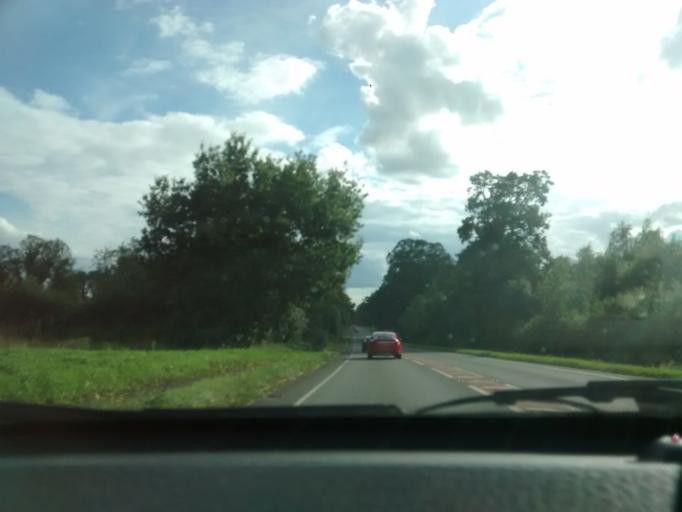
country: GB
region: England
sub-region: Norfolk
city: Downham Market
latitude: 52.6538
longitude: 0.4155
